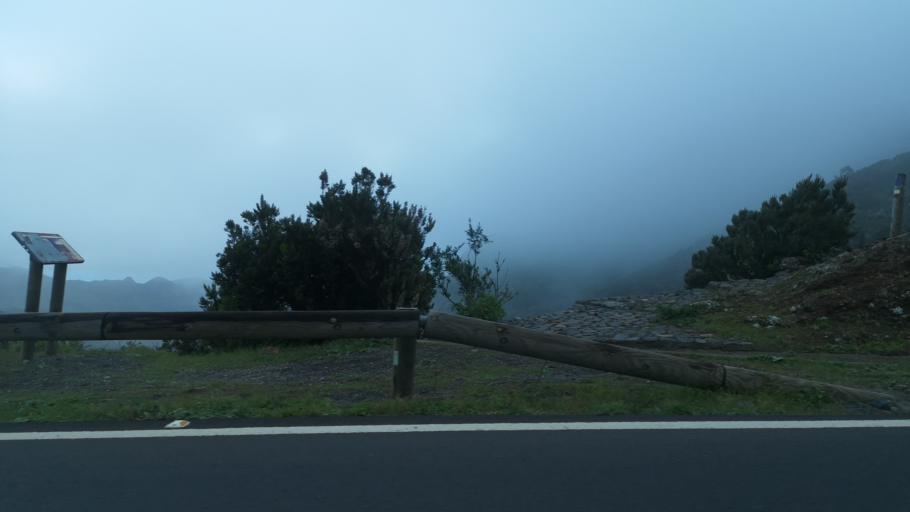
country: ES
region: Canary Islands
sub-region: Provincia de Santa Cruz de Tenerife
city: Alajero
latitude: 28.1040
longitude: -17.2094
